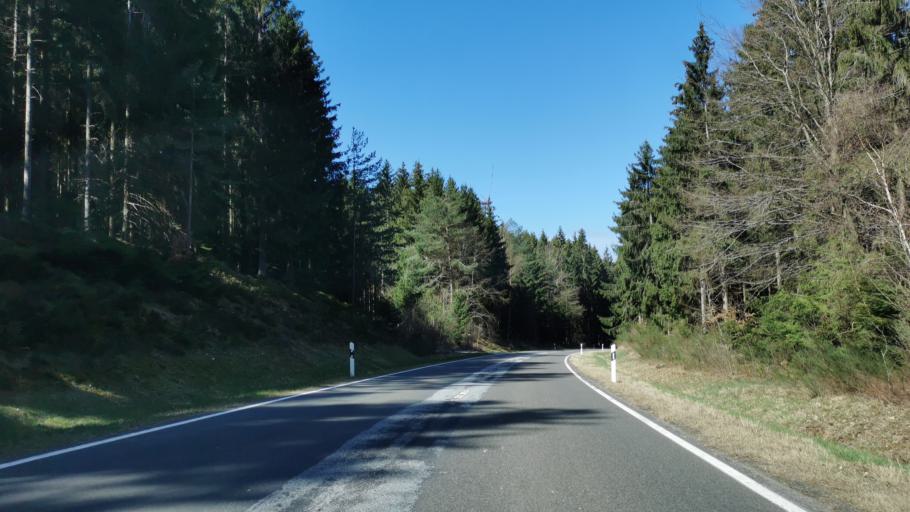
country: DE
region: Rheinland-Pfalz
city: Horath
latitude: 49.8275
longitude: 6.9933
